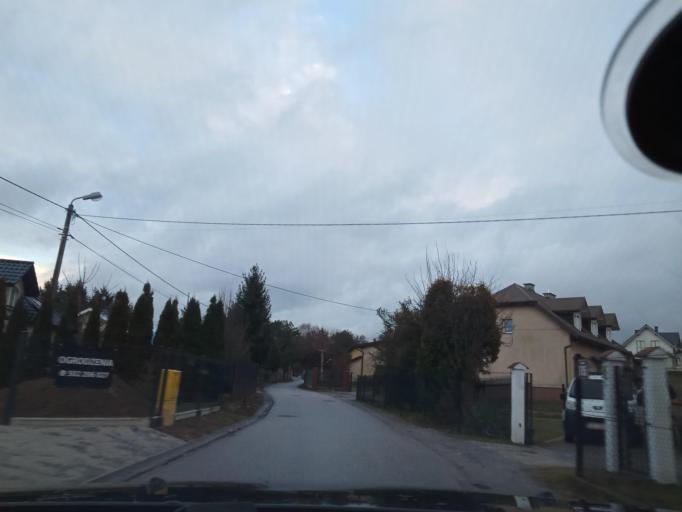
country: PL
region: Lesser Poland Voivodeship
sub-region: Powiat wielicki
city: Kokotow
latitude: 49.9995
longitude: 20.0802
